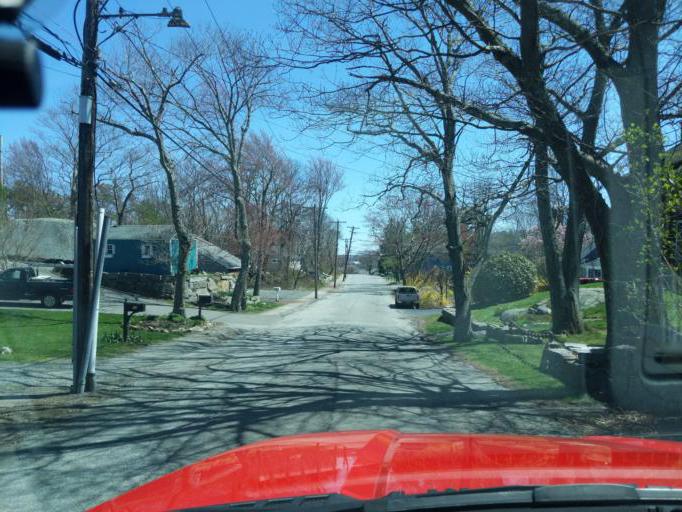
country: US
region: Massachusetts
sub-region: Essex County
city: Rockport
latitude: 42.6771
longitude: -70.6279
